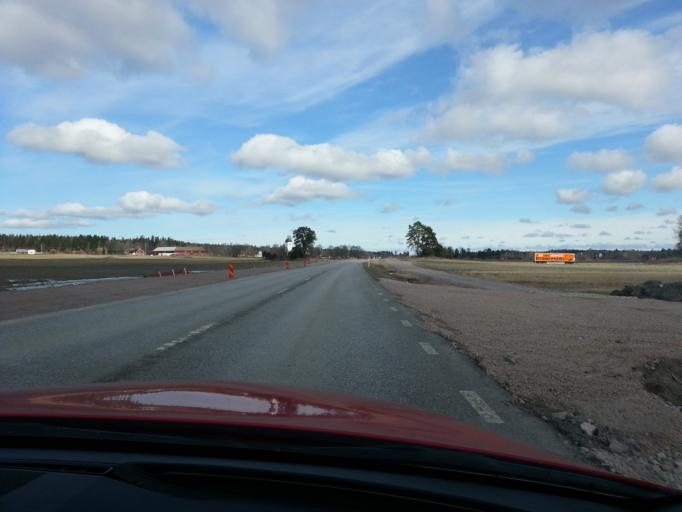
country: SE
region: Uppsala
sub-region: Osthammars Kommun
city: Gimo
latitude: 60.0541
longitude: 18.0586
